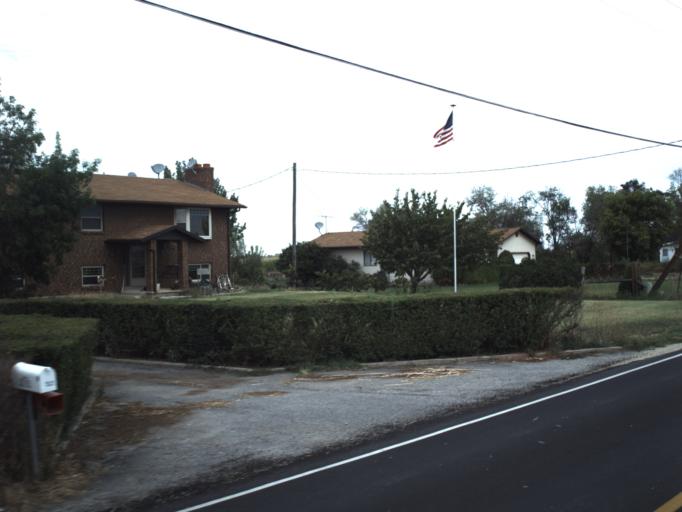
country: US
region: Utah
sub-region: Weber County
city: Plain City
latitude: 41.2480
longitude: -112.0926
